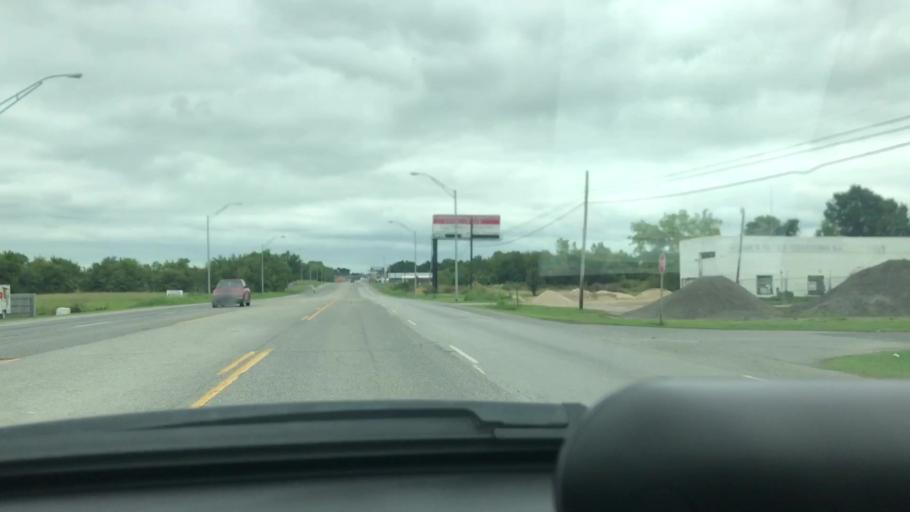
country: US
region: Oklahoma
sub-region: Wagoner County
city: Wagoner
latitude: 35.9480
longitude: -95.3952
